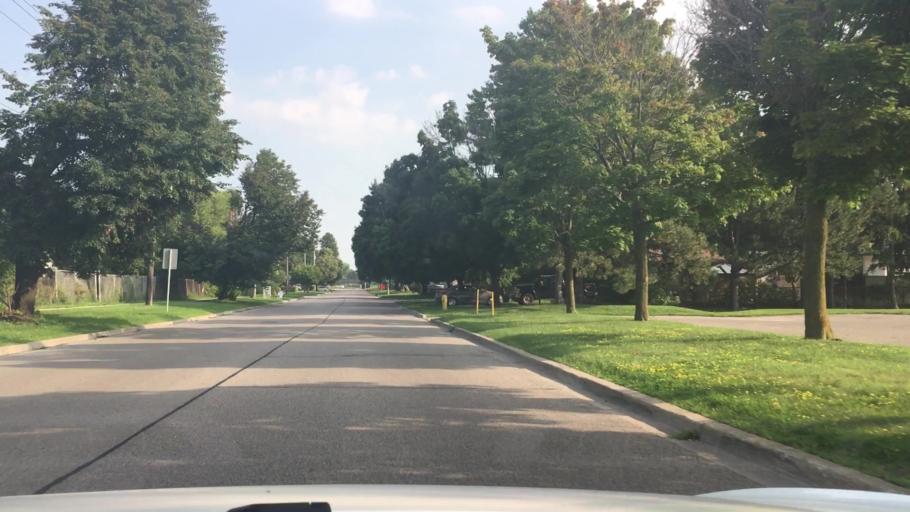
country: CA
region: Ontario
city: Ajax
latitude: 43.8721
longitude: -78.9497
